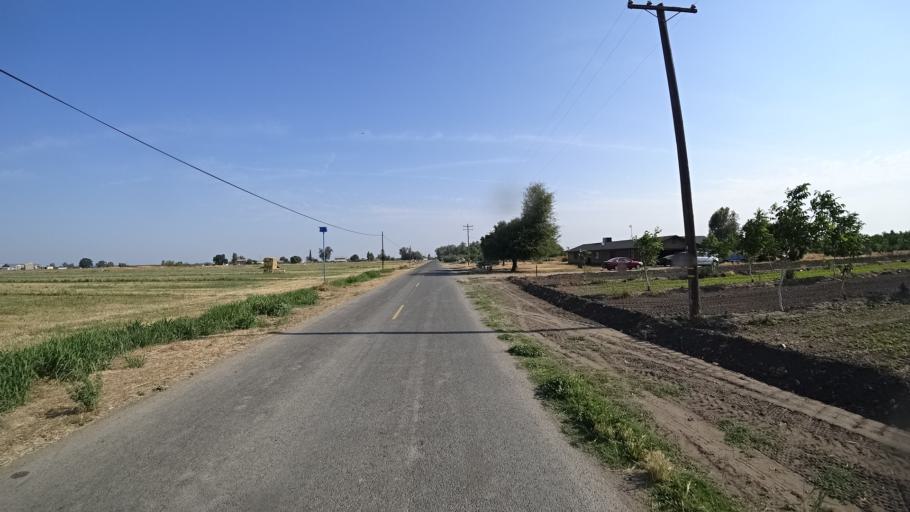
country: US
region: California
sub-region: Fresno County
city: Riverdale
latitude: 36.3754
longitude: -119.8162
